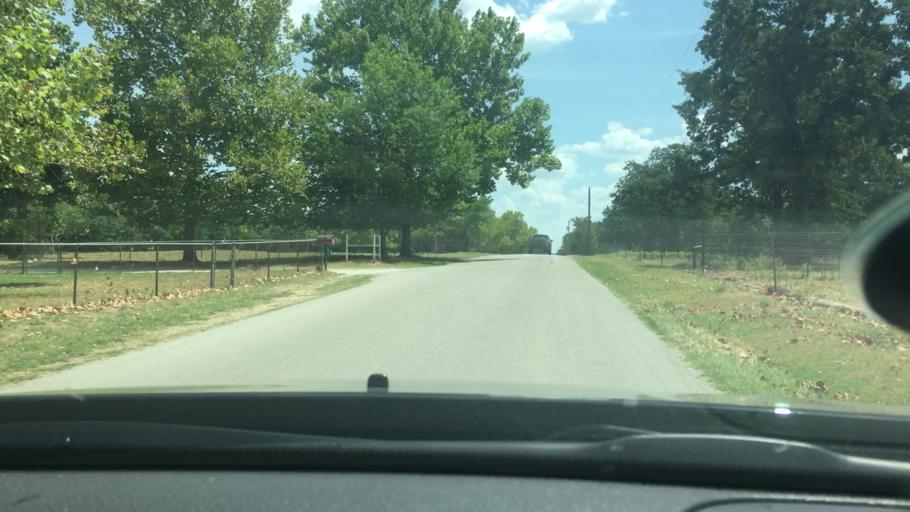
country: US
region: Oklahoma
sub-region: Carter County
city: Ardmore
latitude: 34.0710
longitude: -97.1934
